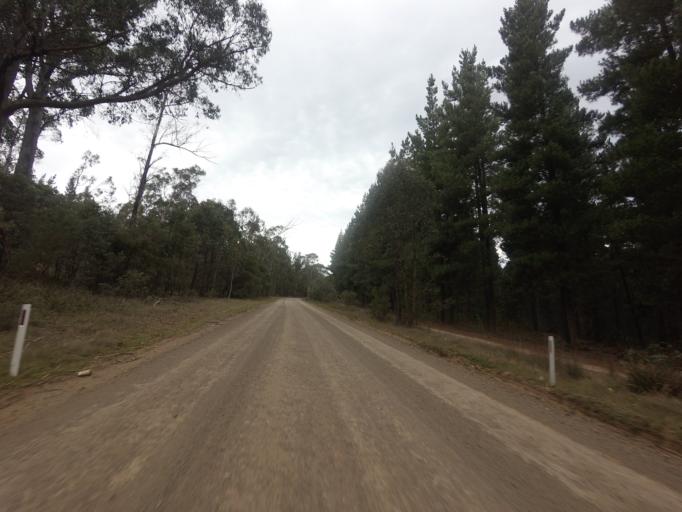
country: AU
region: Tasmania
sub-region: Derwent Valley
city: New Norfolk
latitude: -42.5715
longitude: 146.9912
